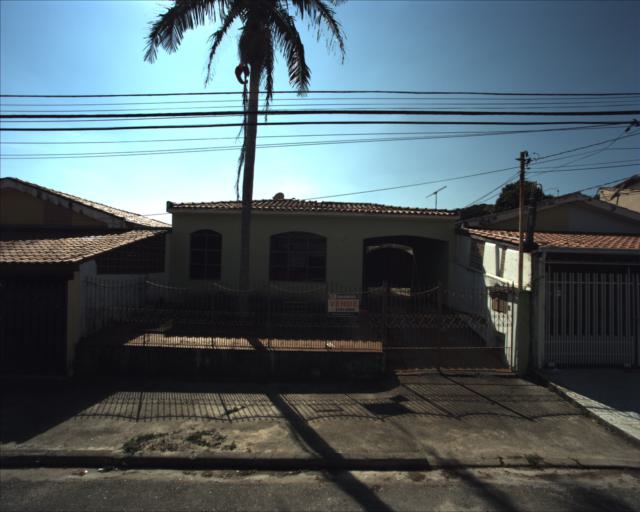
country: BR
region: Sao Paulo
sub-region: Sorocaba
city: Sorocaba
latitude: -23.4720
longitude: -47.4381
